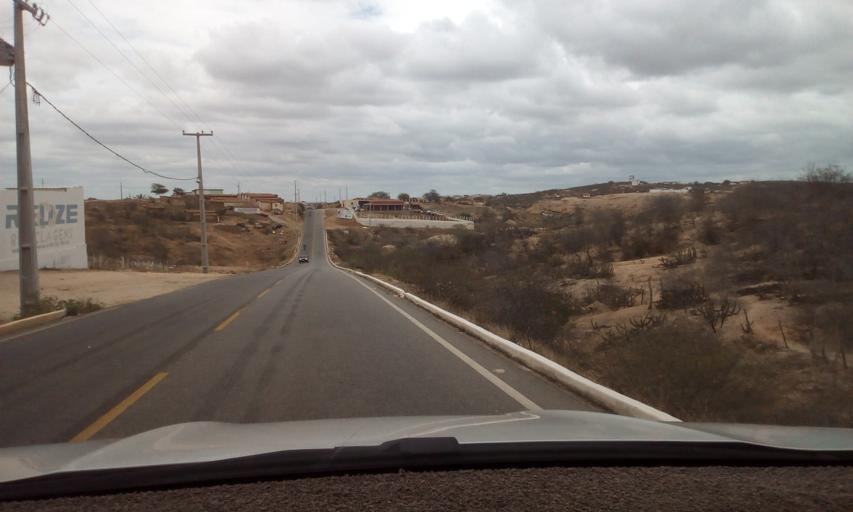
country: BR
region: Paraiba
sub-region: Picui
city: Picui
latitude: -6.5185
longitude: -36.3321
